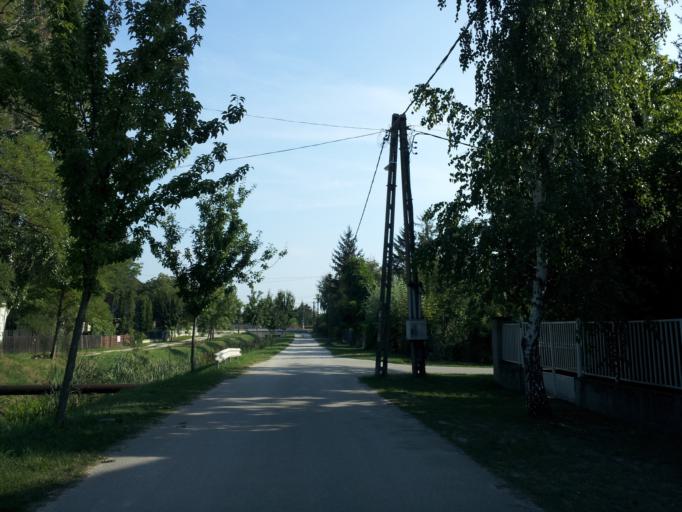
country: HU
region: Somogy
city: Zamardi
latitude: 46.8904
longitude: 17.9811
